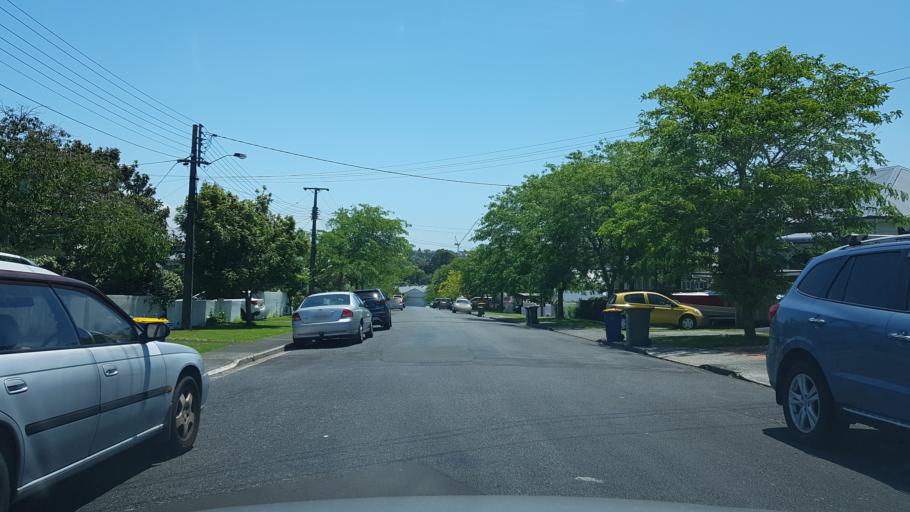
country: NZ
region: Auckland
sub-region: Auckland
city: Auckland
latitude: -36.8283
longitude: 174.7913
